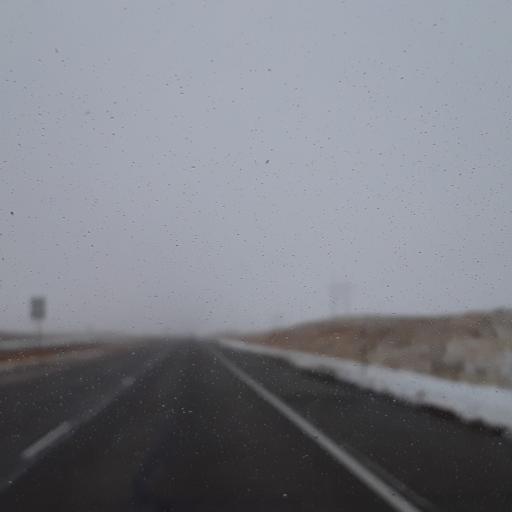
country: US
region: Nebraska
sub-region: Cheyenne County
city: Sidney
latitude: 40.7964
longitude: -102.8770
